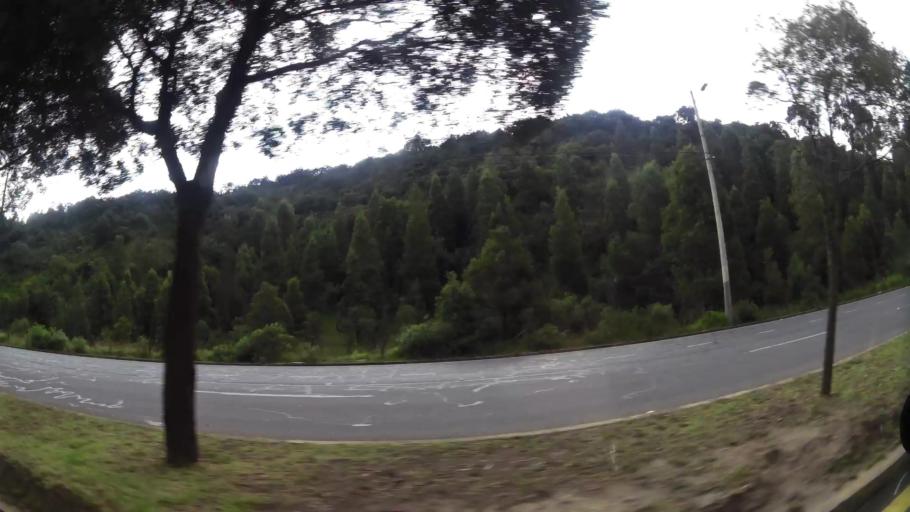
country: EC
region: Pichincha
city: Sangolqui
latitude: -0.3347
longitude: -78.5200
